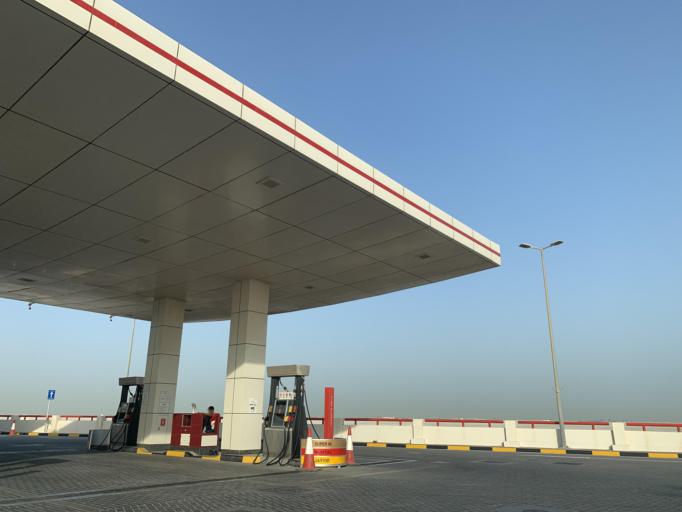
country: BH
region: Muharraq
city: Al Muharraq
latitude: 26.2818
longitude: 50.5969
